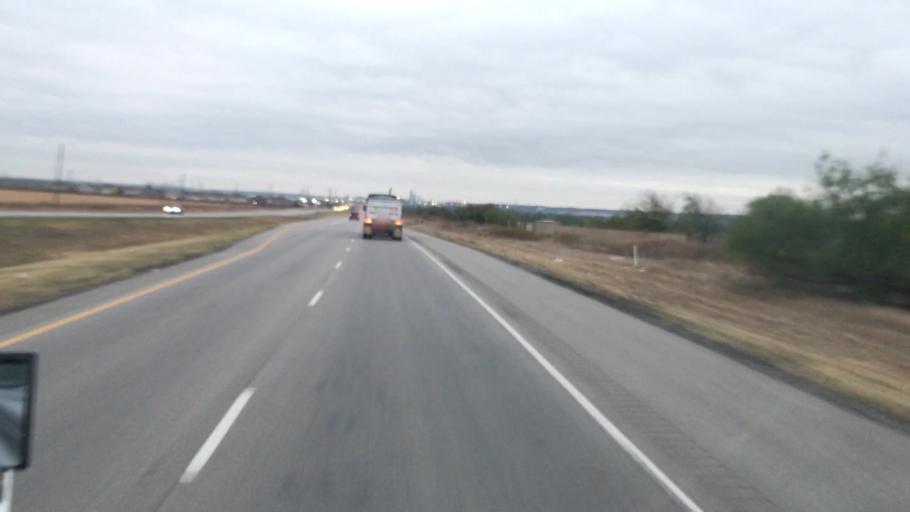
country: US
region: Texas
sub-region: Johnson County
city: Venus
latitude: 32.4375
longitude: -97.0972
